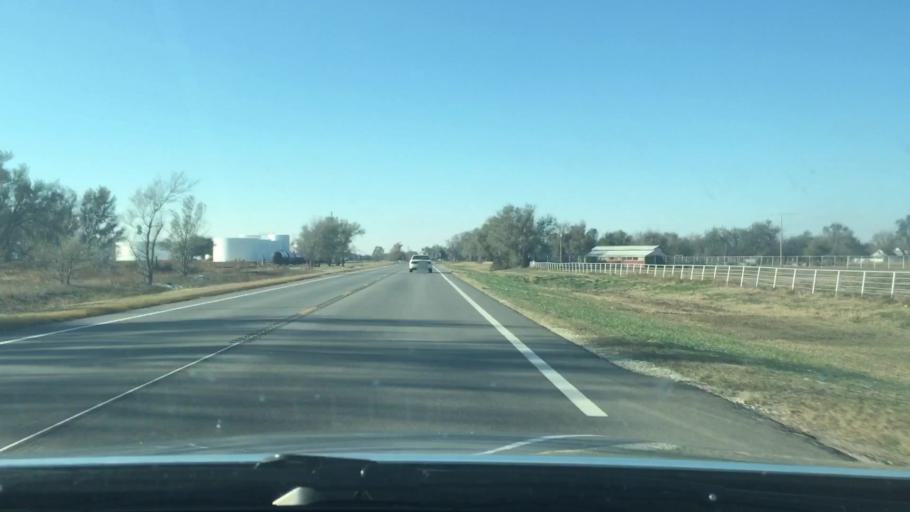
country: US
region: Kansas
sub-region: Reno County
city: Nickerson
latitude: 38.1406
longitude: -98.0738
